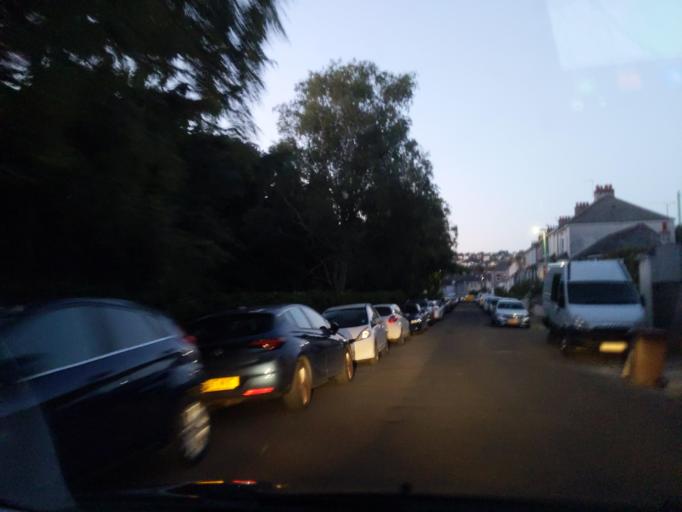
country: GB
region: England
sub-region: Plymouth
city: Plymouth
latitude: 50.3862
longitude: -4.1455
